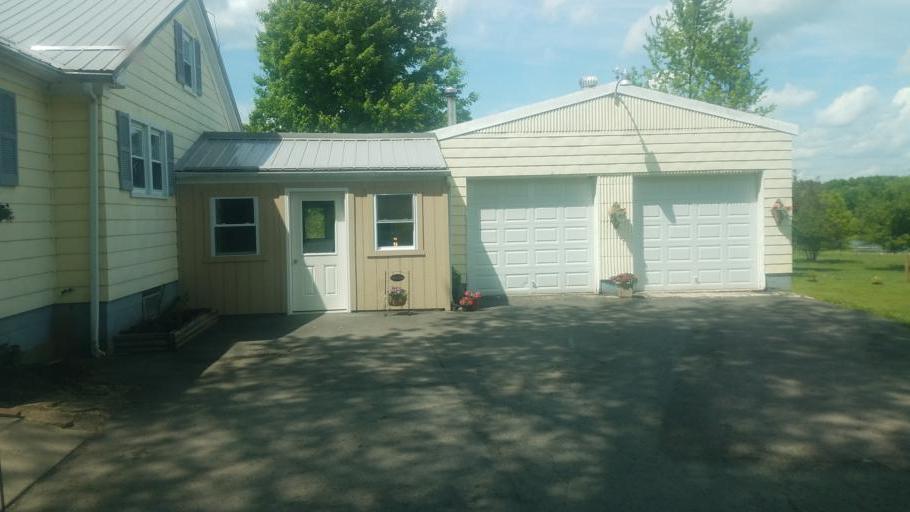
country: US
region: Pennsylvania
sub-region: Venango County
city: Franklin
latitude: 41.2263
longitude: -79.8322
